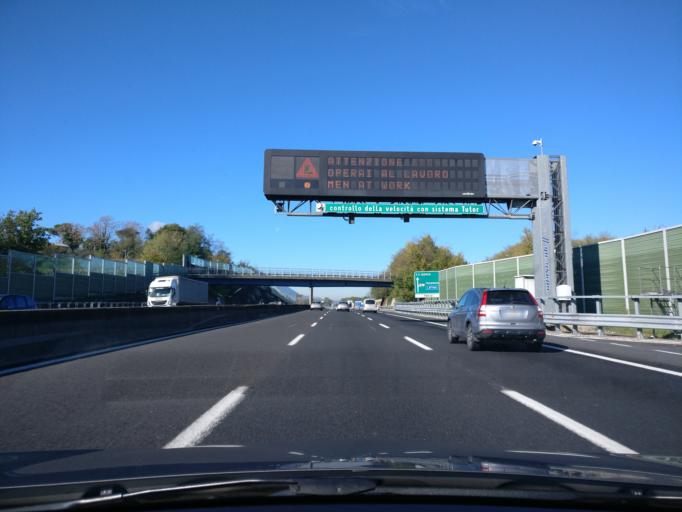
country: IT
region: Latium
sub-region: Provincia di Frosinone
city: Frosinone
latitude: 41.6159
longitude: 13.3231
